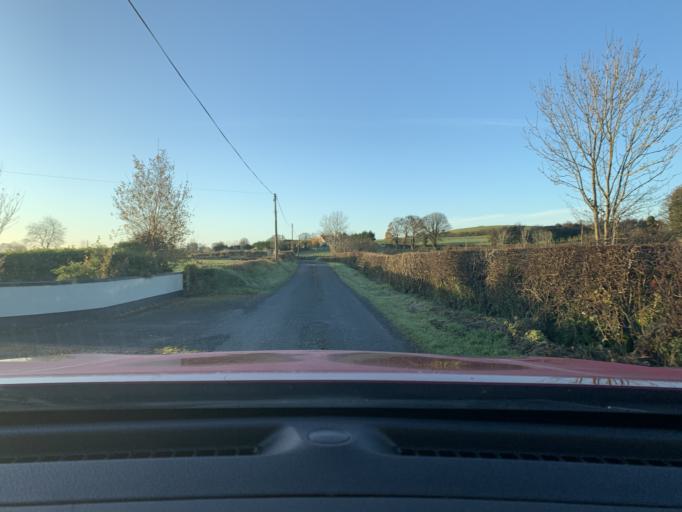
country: IE
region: Connaught
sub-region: Sligo
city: Ballymote
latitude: 54.0680
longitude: -8.5518
